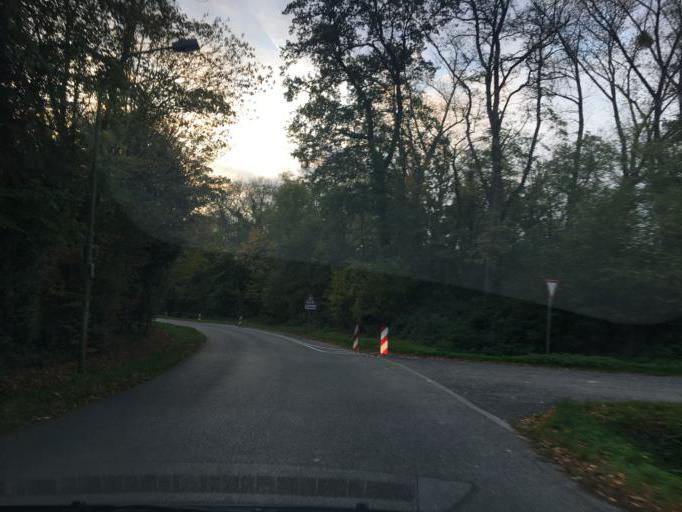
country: DE
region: North Rhine-Westphalia
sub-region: Regierungsbezirk Koln
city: Norvenich
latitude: 50.7642
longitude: 6.6459
